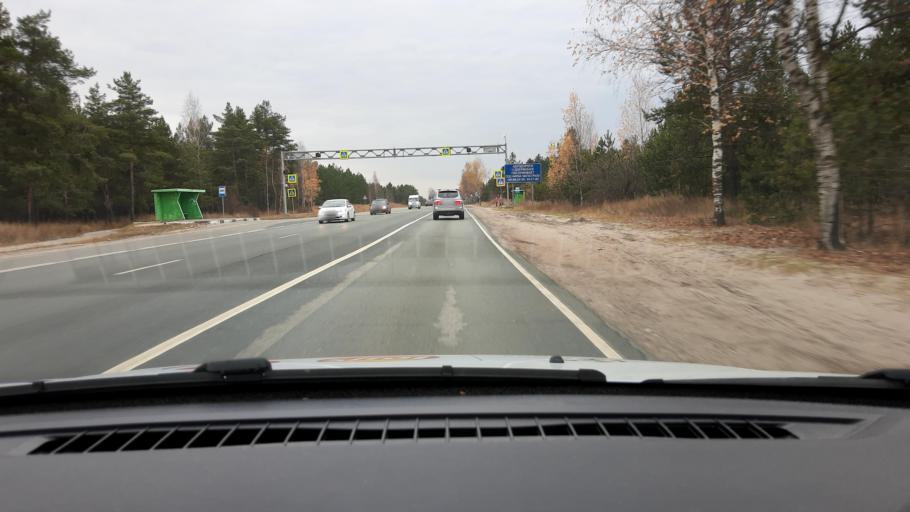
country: RU
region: Nizjnij Novgorod
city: Dzerzhinsk
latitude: 56.2923
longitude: 43.4760
